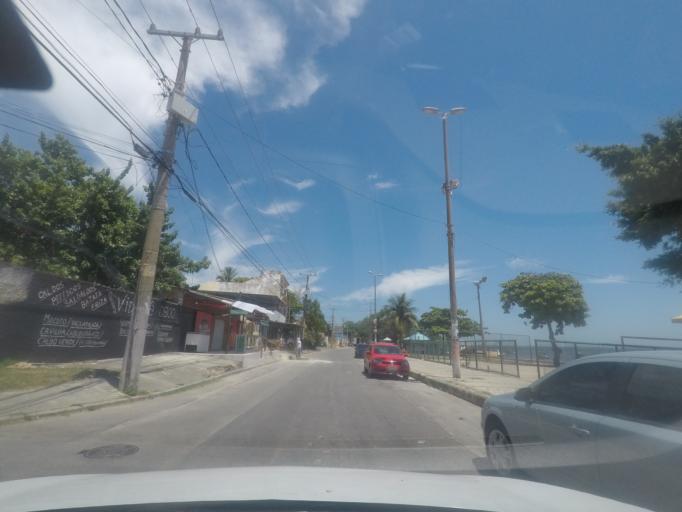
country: BR
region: Rio de Janeiro
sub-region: Itaguai
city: Itaguai
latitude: -22.9869
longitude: -43.6926
